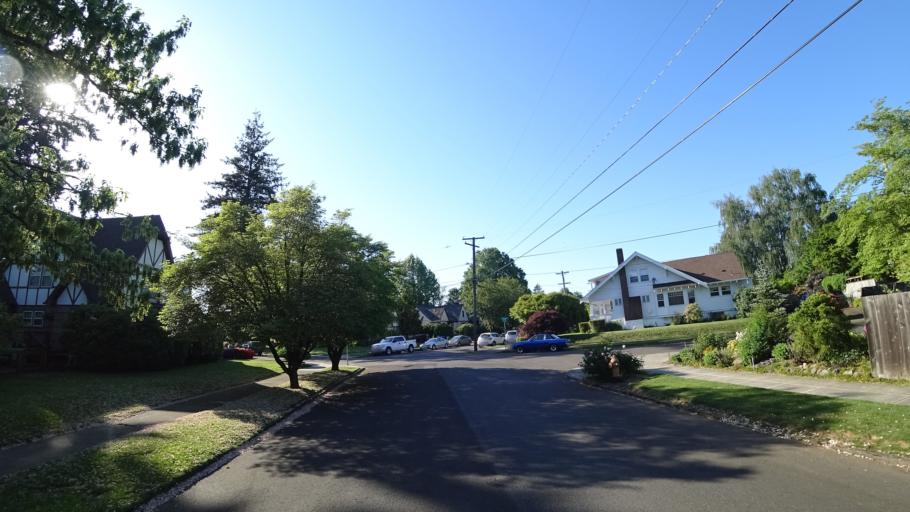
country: US
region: Oregon
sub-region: Multnomah County
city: Portland
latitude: 45.5531
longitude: -122.6879
